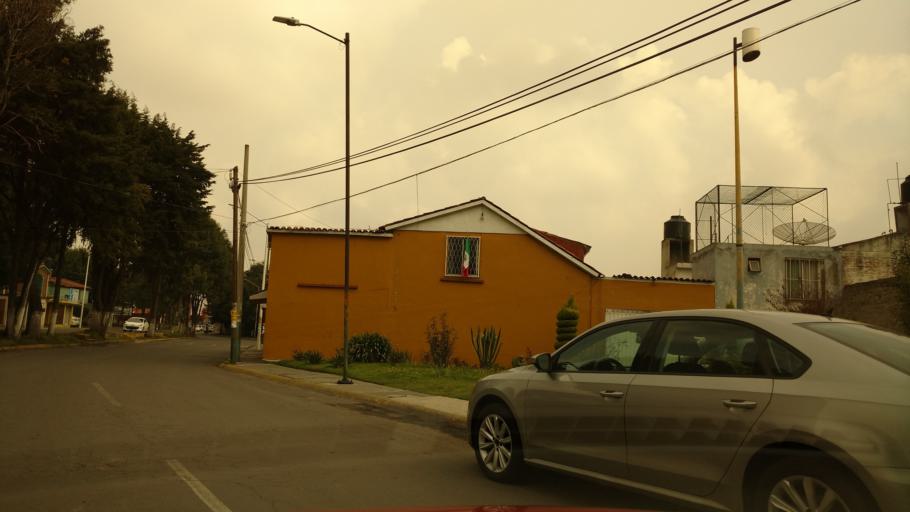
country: MX
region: Mexico
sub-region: Metepec
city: San Jorge Pueblo Nuevo
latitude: 19.2584
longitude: -99.6352
